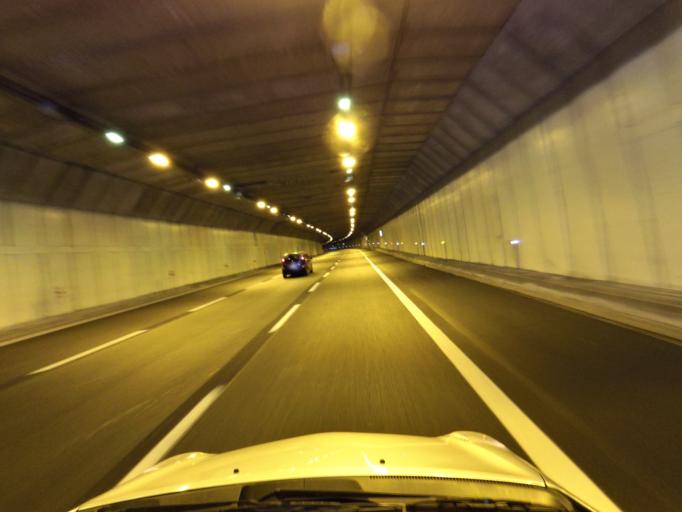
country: IT
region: Emilia-Romagna
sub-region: Provincia di Bologna
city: Vado
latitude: 44.2980
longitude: 11.2349
